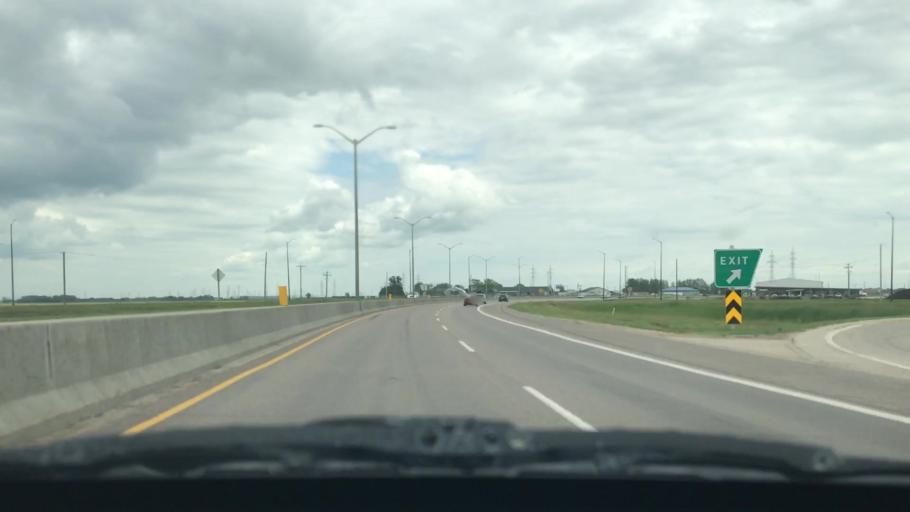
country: CA
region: Manitoba
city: Winnipeg
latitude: 49.8560
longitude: -97.0161
